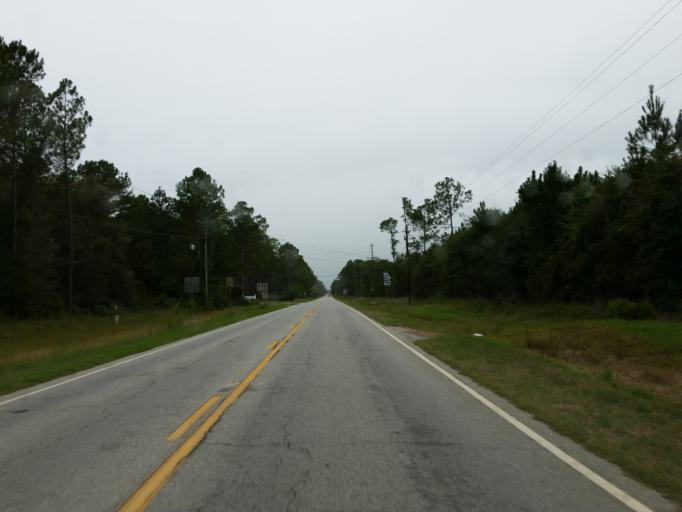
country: US
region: Georgia
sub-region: Lanier County
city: Lakeland
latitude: 31.0436
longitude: -83.1004
